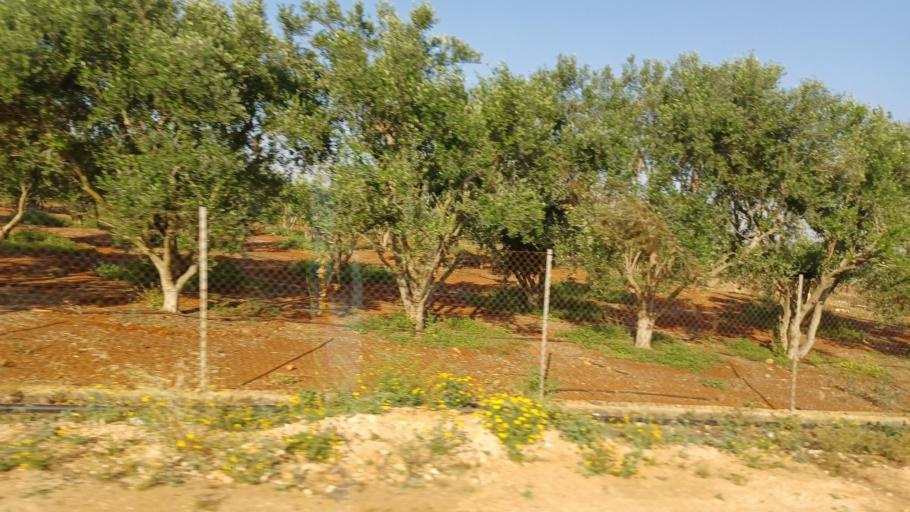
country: CY
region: Ammochostos
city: Frenaros
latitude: 35.0582
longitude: 33.9075
